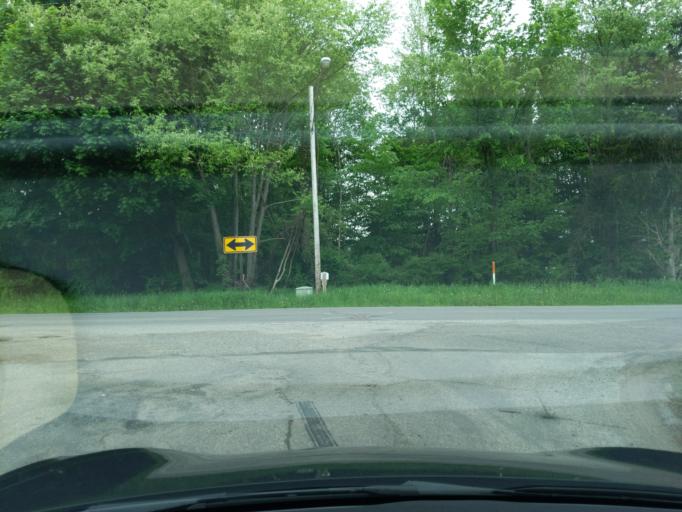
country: US
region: Michigan
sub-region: Ingham County
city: Leslie
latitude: 42.3803
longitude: -84.3295
